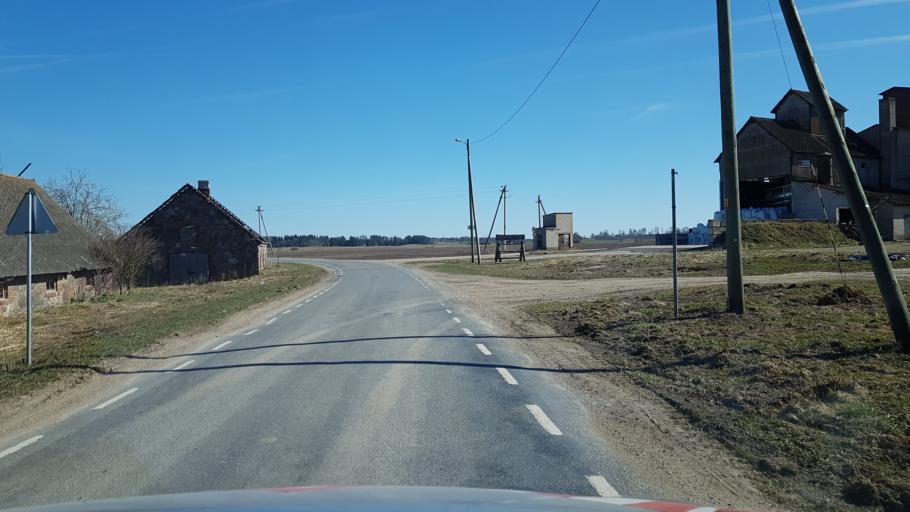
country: EE
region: Laeaene-Virumaa
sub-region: Someru vald
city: Someru
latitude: 59.3401
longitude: 26.5129
